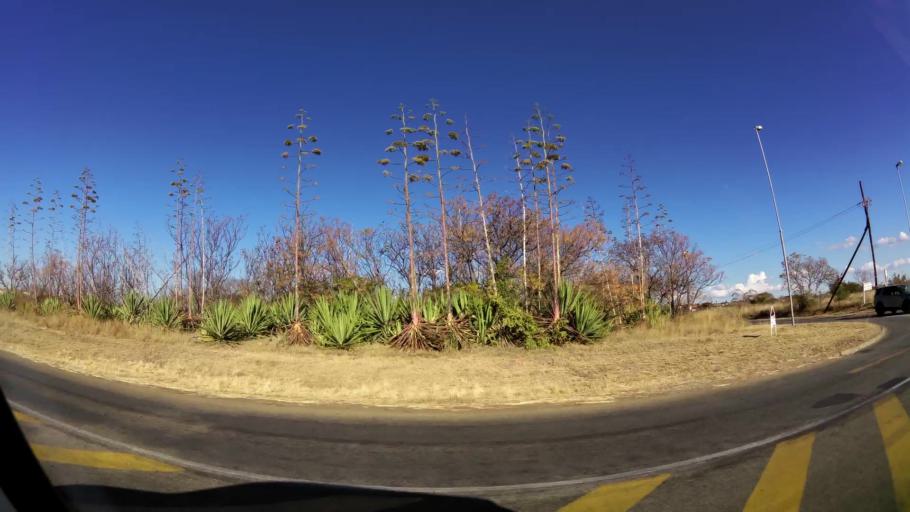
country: ZA
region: Limpopo
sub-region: Capricorn District Municipality
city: Polokwane
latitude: -23.8752
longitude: 29.4794
